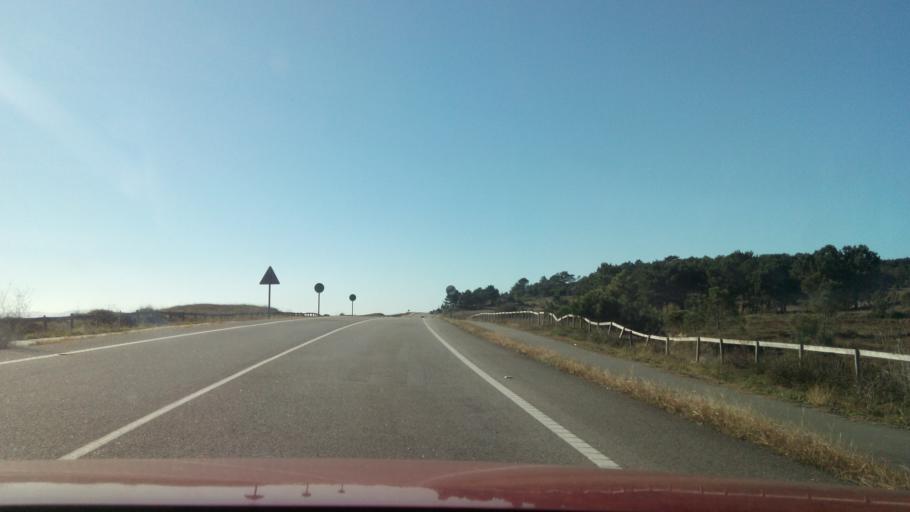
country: ES
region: Galicia
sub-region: Provincia de Pontevedra
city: O Grove
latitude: 42.4626
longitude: -8.8754
